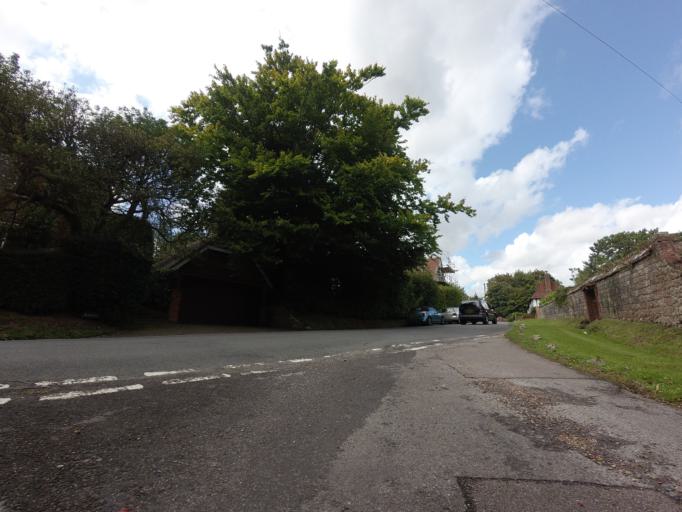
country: GB
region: England
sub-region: Kent
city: Borough Green
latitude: 51.2618
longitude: 0.2953
